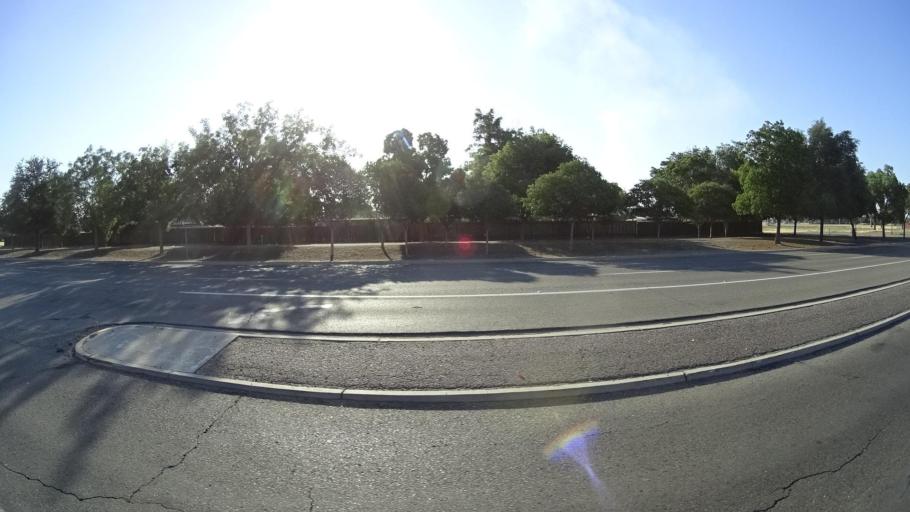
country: US
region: California
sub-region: Fresno County
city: Tarpey Village
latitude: 36.7910
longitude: -119.7004
